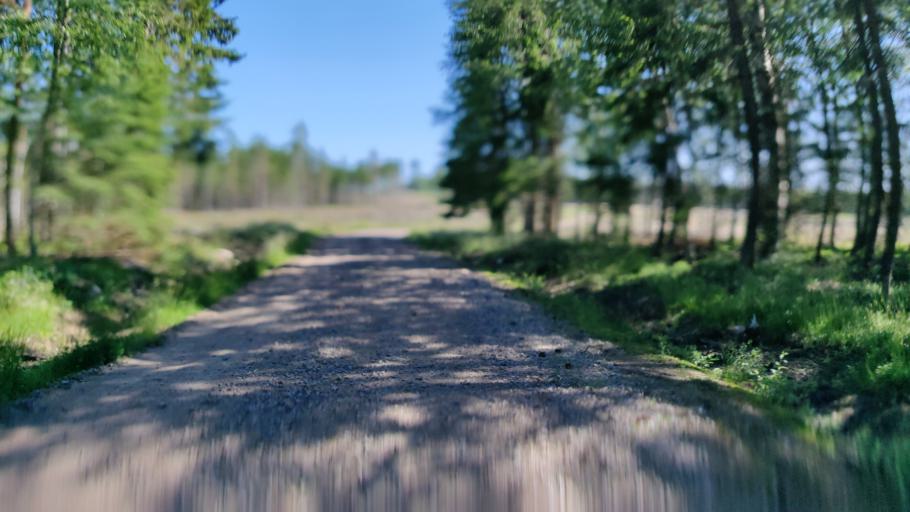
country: SE
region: Vaermland
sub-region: Hagfors Kommun
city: Hagfors
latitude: 59.9743
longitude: 13.6023
